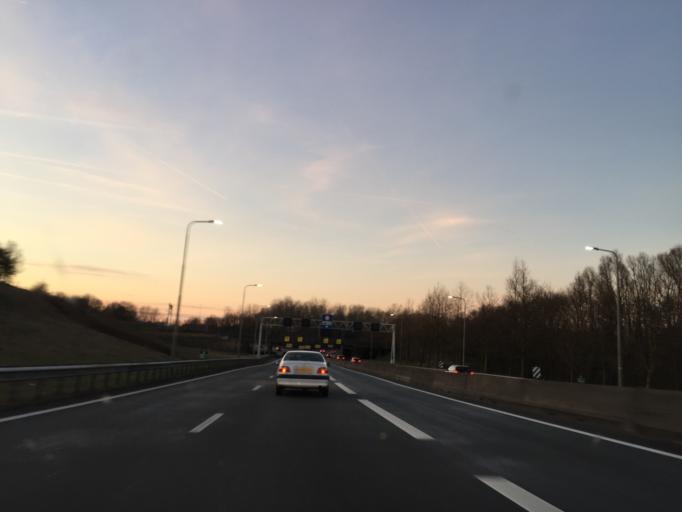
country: NL
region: South Holland
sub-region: Gemeente Rotterdam
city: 's-Gravenland
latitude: 51.9471
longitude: 4.5320
